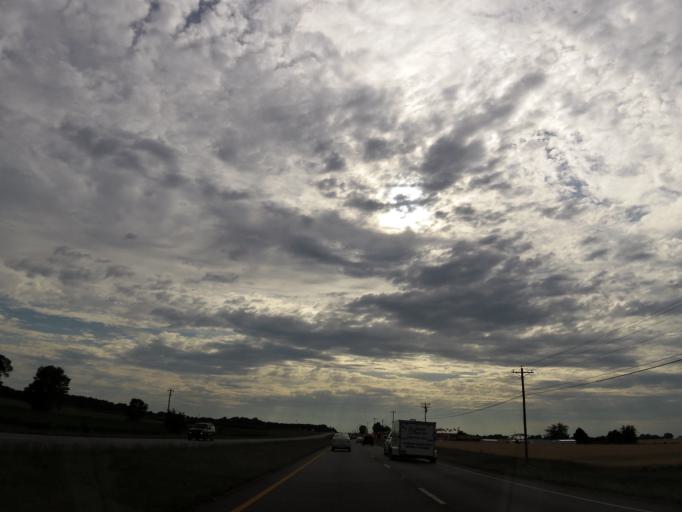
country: US
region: Alabama
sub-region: Morgan County
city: Decatur
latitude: 34.6284
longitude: -86.9275
